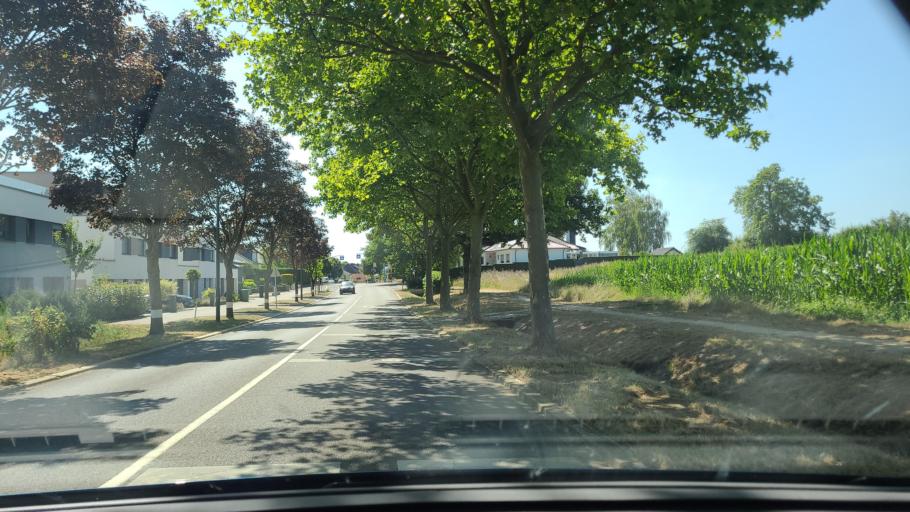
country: LU
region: Luxembourg
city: Schouweiler
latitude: 49.5893
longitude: 5.9514
